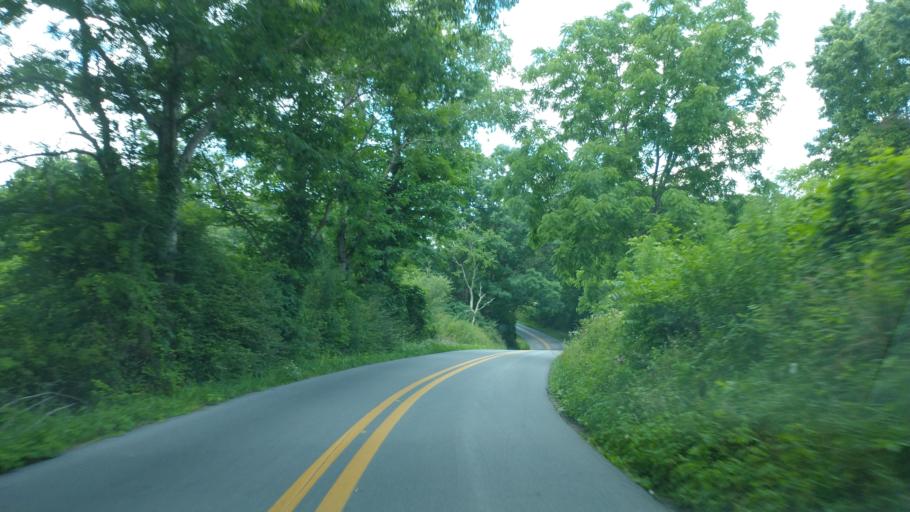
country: US
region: West Virginia
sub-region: Mercer County
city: Athens
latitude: 37.4375
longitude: -81.0624
